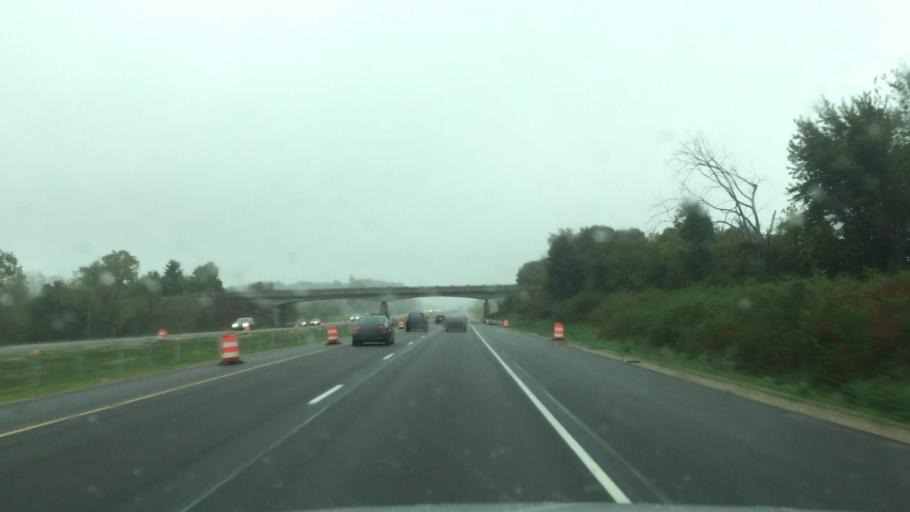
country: US
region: Michigan
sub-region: Van Buren County
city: Hartford
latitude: 42.1969
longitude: -86.0733
